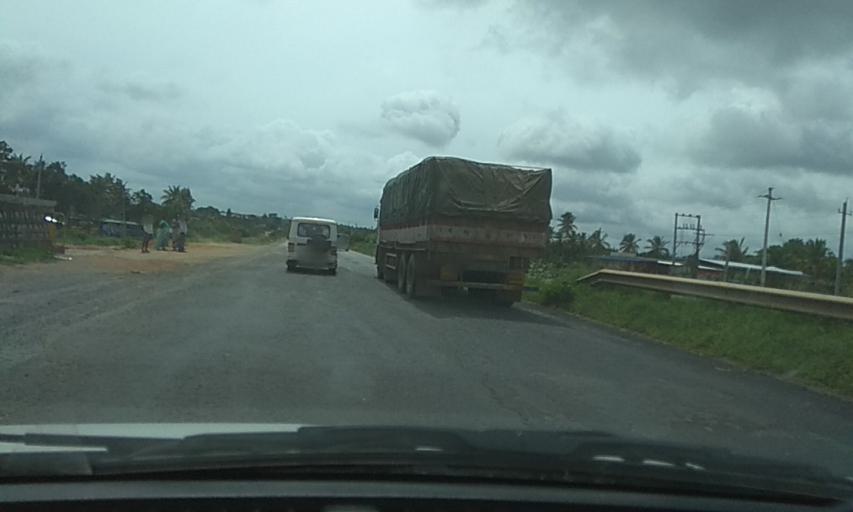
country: IN
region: Karnataka
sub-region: Davanagere
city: Mayakonda
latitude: 14.3926
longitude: 76.0467
